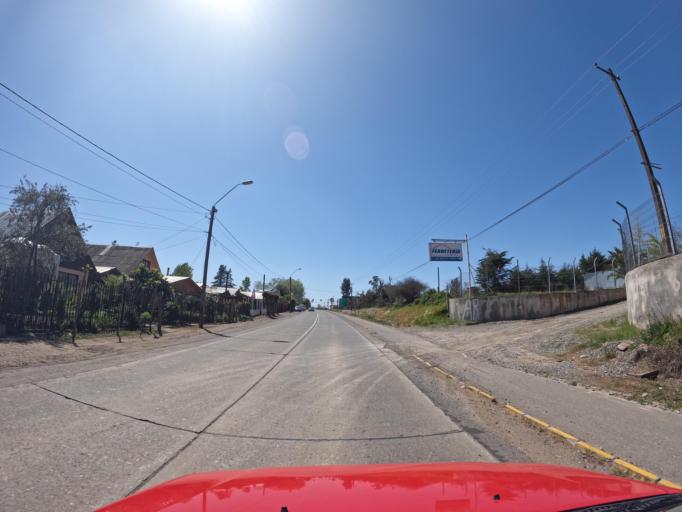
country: CL
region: Maule
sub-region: Provincia de Linares
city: Colbun
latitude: -35.7645
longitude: -71.4221
